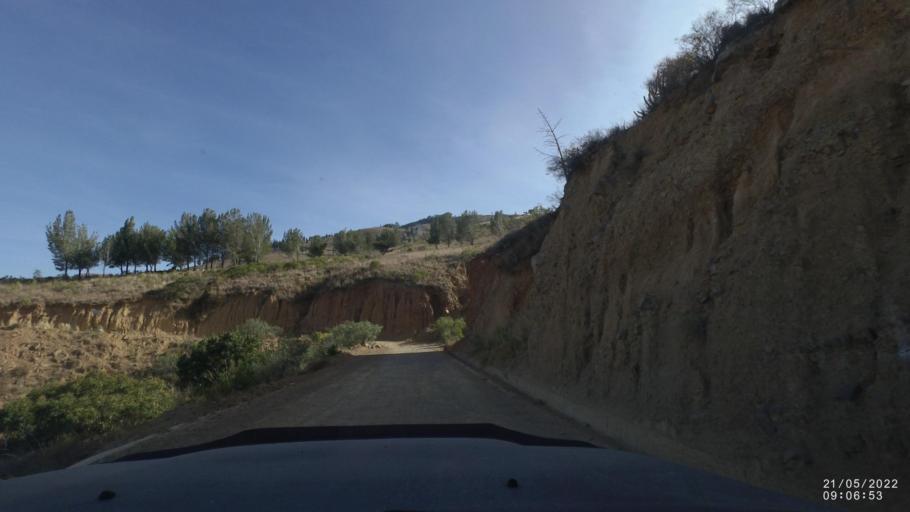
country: BO
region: Cochabamba
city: Cochabamba
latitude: -17.3772
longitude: -66.0247
